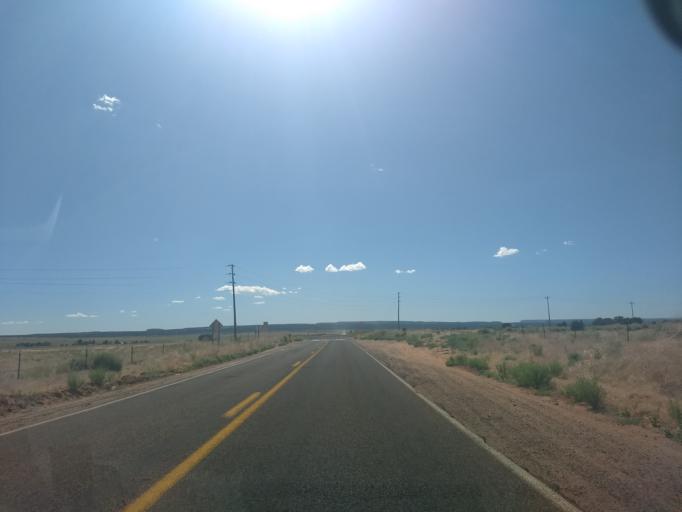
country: US
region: Arizona
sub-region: Mohave County
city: Colorado City
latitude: 36.9469
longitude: -112.9546
